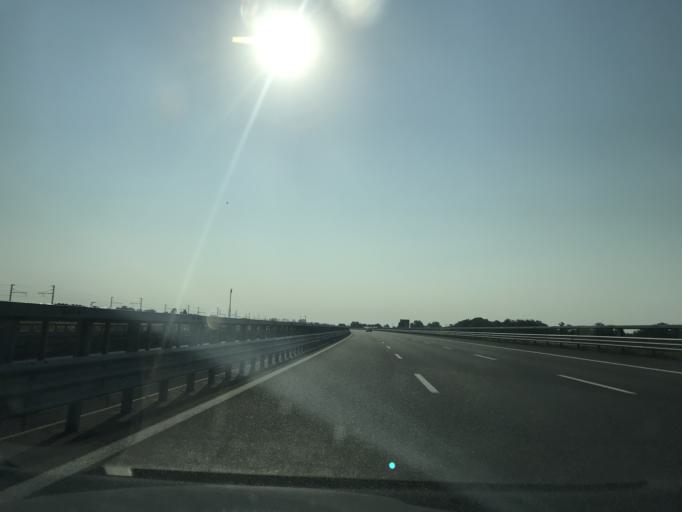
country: IT
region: Lombardy
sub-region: Provincia di Bergamo
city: Calvenzano
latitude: 45.5033
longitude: 9.5863
